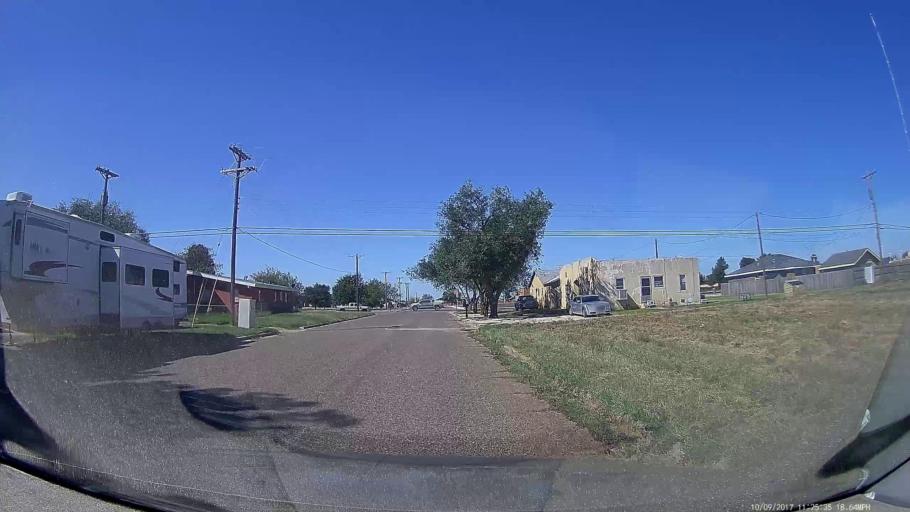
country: US
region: New Mexico
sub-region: Curry County
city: Clovis
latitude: 34.4110
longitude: -103.2223
